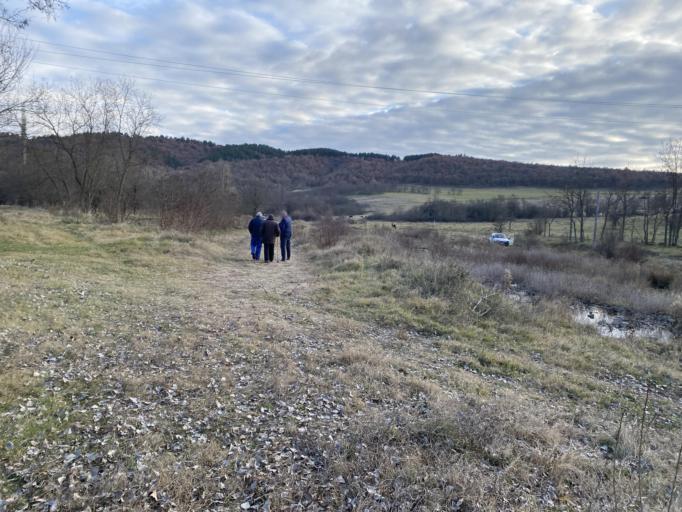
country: MK
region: Opstina Rankovce
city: Rankovce
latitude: 42.1545
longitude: 22.0816
